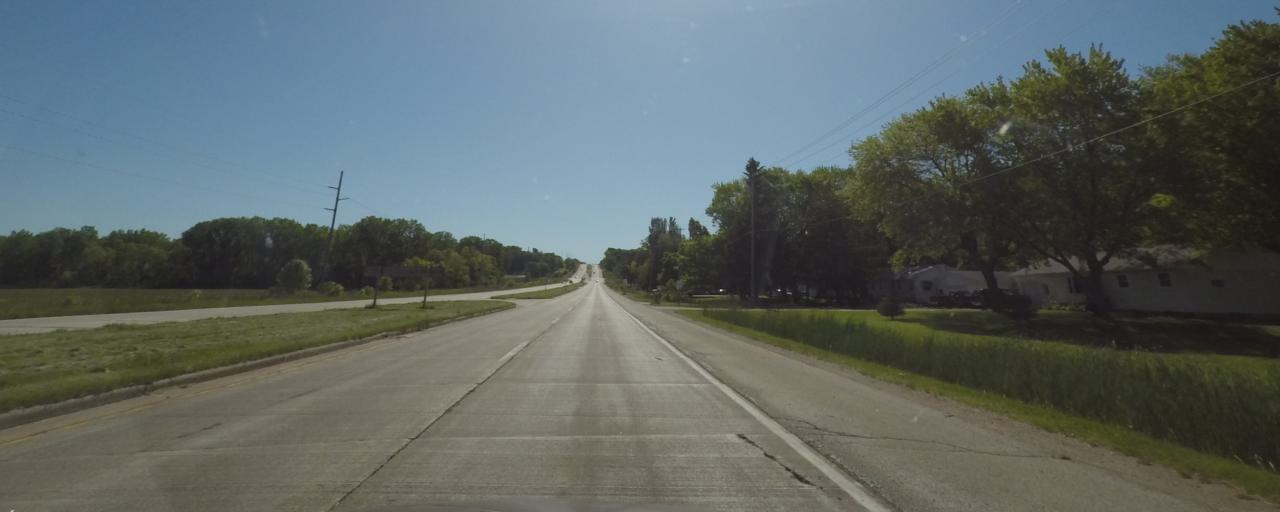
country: US
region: Wisconsin
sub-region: Fond du Lac County
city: Fond du Lac
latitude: 43.7837
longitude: -88.3948
